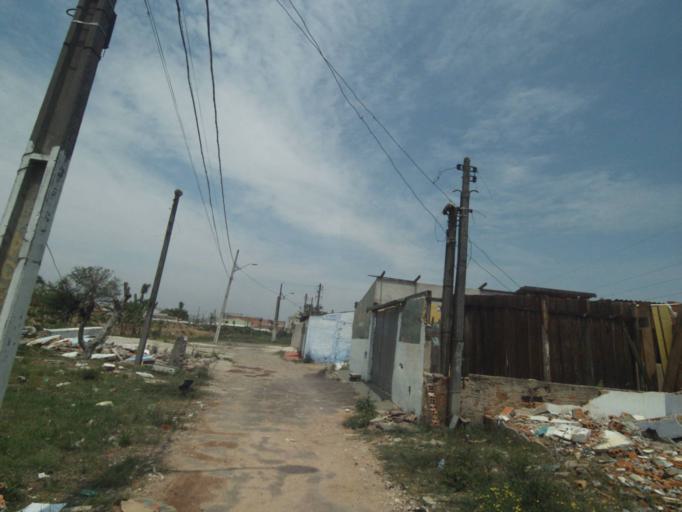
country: BR
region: Parana
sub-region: Pinhais
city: Pinhais
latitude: -25.4259
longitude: -49.1986
